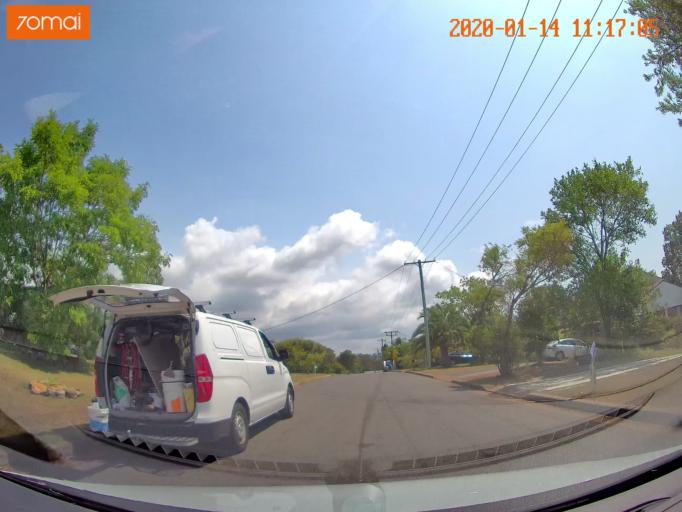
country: AU
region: New South Wales
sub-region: Lake Macquarie Shire
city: Cooranbong
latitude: -33.0959
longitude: 151.4618
